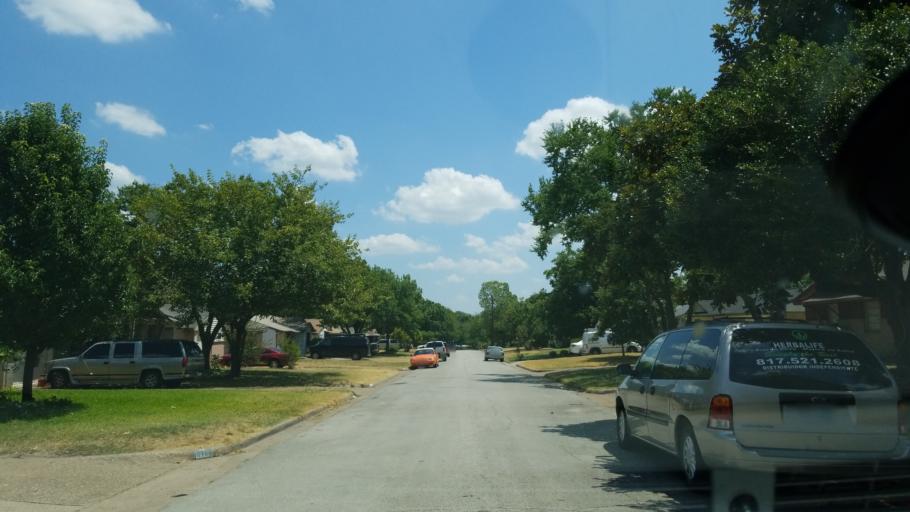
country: US
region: Texas
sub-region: Dallas County
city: Duncanville
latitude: 32.6680
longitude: -96.9003
